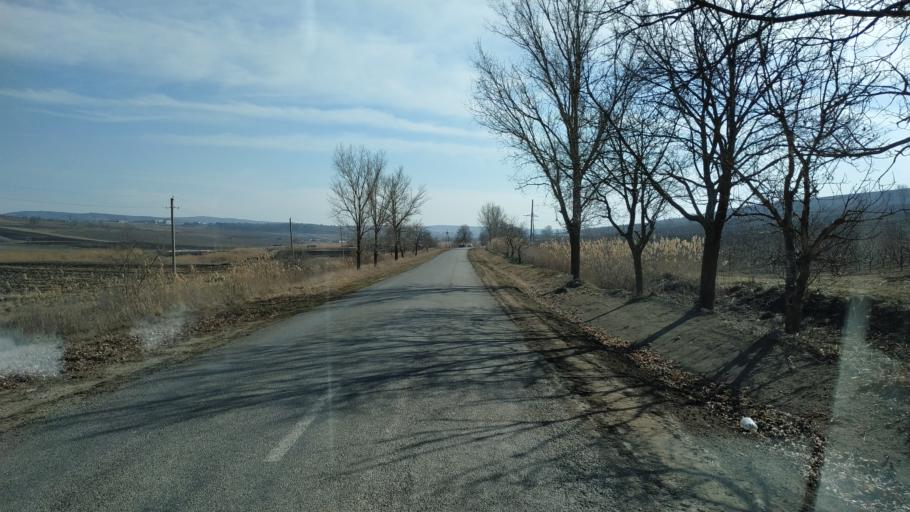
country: MD
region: Nisporeni
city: Nisporeni
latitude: 47.0956
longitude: 28.1331
